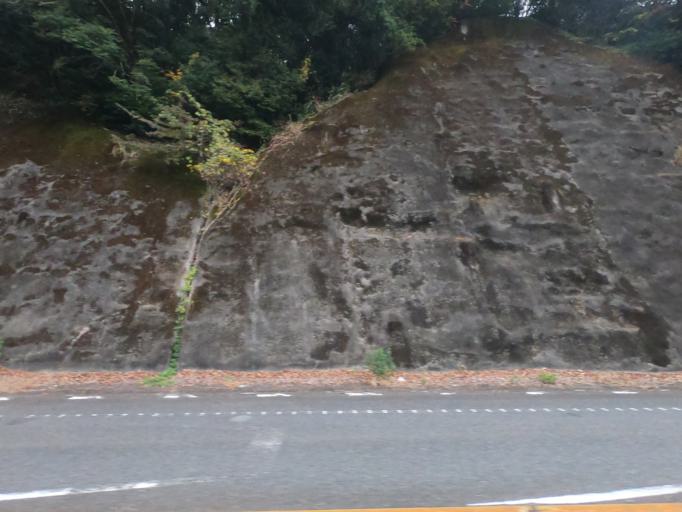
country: JP
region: Kumamoto
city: Minamata
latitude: 32.2489
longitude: 130.5017
